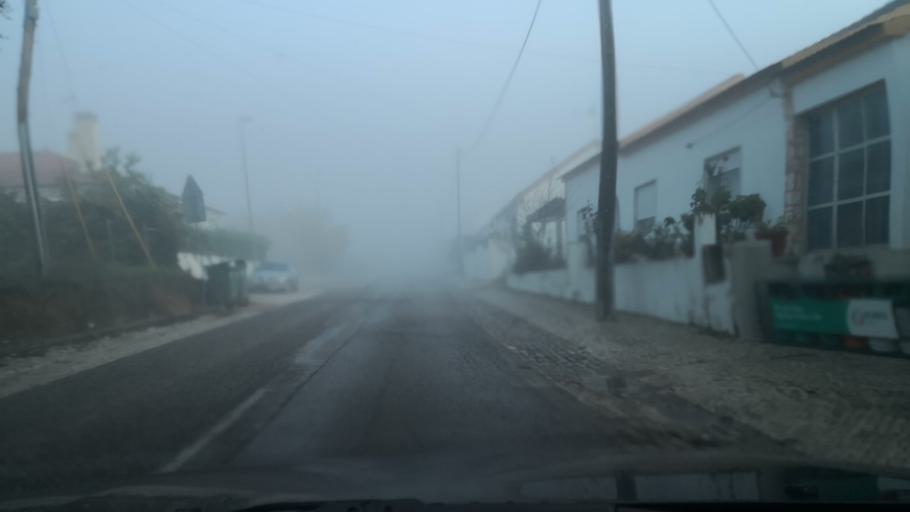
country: PT
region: Setubal
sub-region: Palmela
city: Palmela
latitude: 38.5673
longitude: -8.8355
